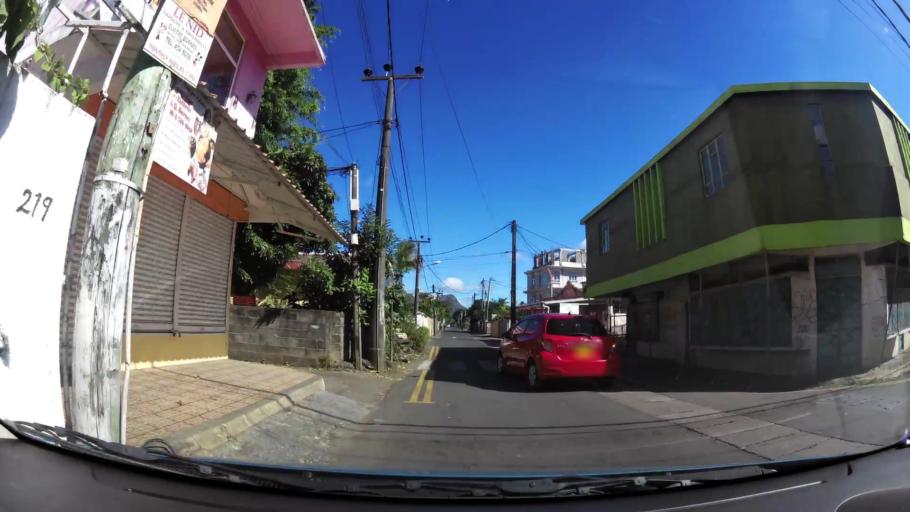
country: MU
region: Plaines Wilhems
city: Quatre Bornes
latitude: -20.2793
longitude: 57.4684
